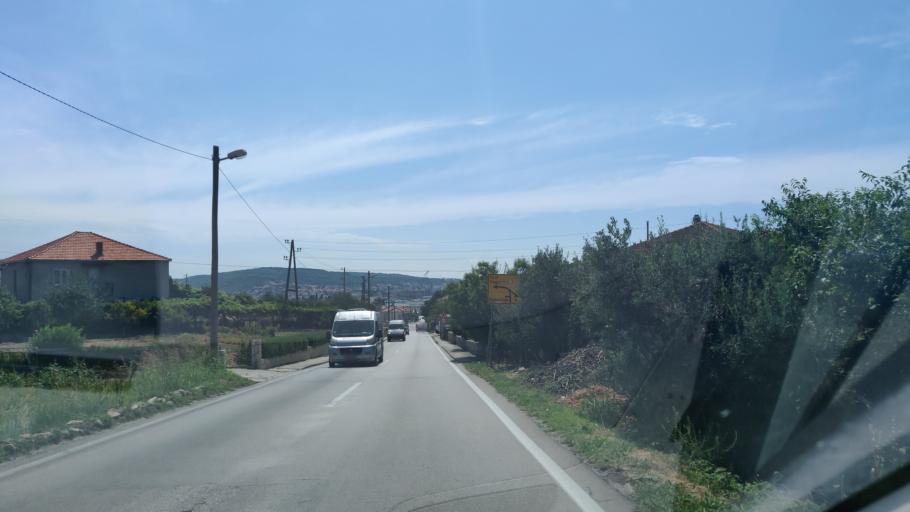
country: HR
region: Splitsko-Dalmatinska
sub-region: Grad Trogir
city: Trogir
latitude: 43.5202
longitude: 16.2267
